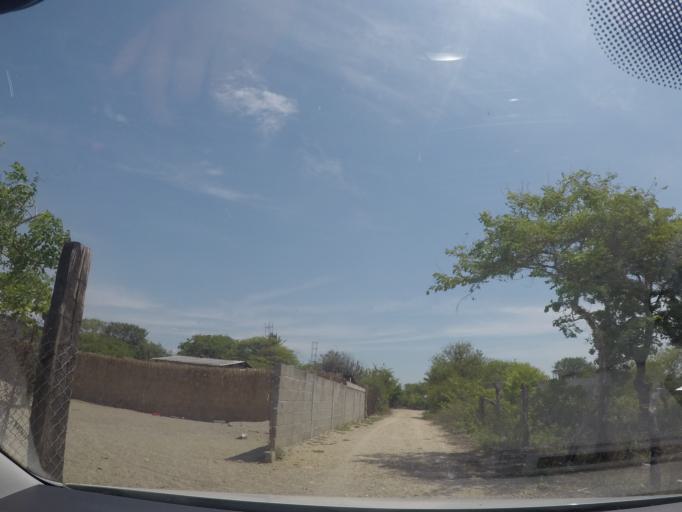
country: MX
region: Oaxaca
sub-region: Salina Cruz
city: Salina Cruz
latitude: 16.1911
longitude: -95.1161
